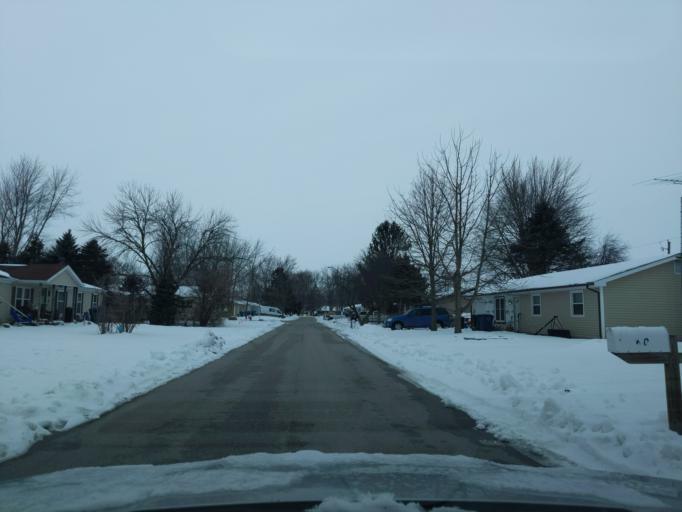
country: US
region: Indiana
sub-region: Benton County
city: Otterbein
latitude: 40.4837
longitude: -87.0918
